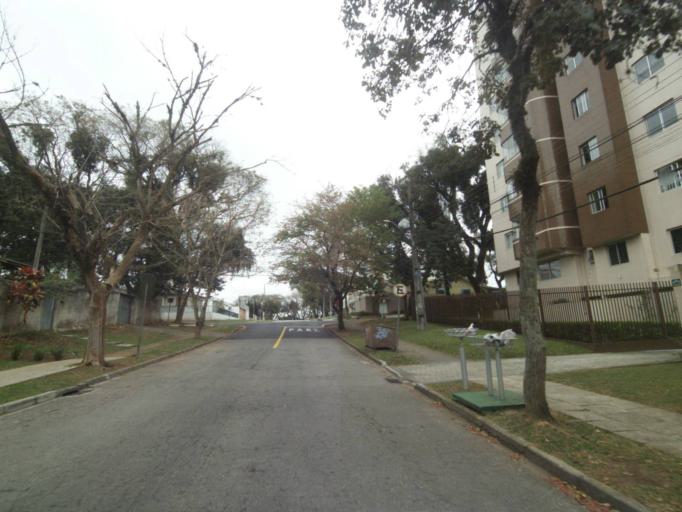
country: BR
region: Parana
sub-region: Curitiba
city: Curitiba
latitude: -25.4551
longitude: -49.2962
